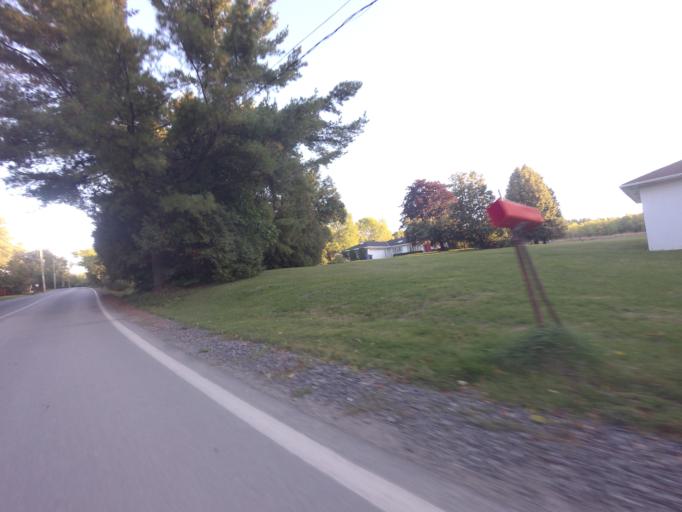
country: CA
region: Quebec
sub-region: Monteregie
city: Hudson
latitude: 45.4728
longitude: -74.1828
